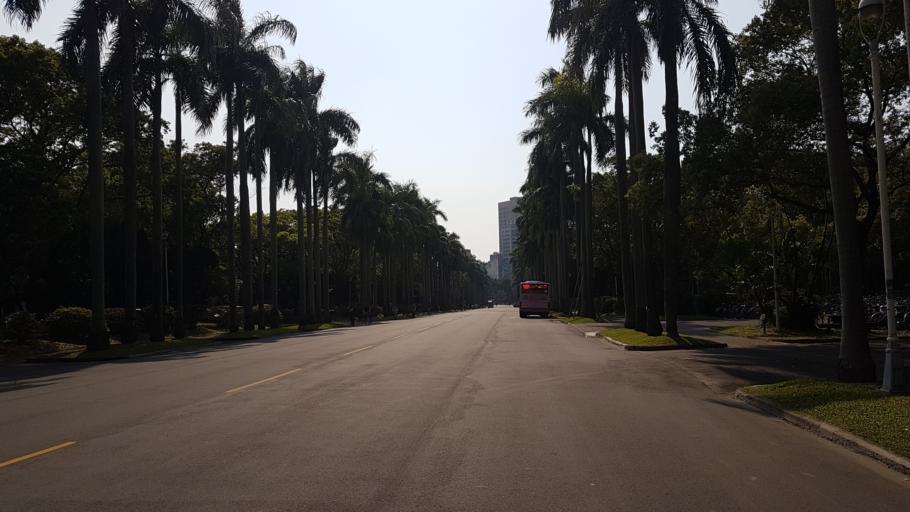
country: TW
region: Taipei
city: Taipei
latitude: 25.0173
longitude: 121.5386
